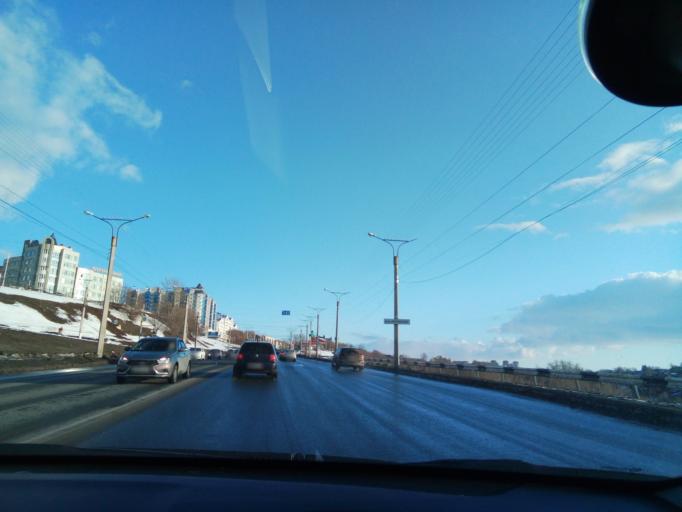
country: RU
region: Chuvashia
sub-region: Cheboksarskiy Rayon
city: Cheboksary
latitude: 56.1337
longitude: 47.2402
